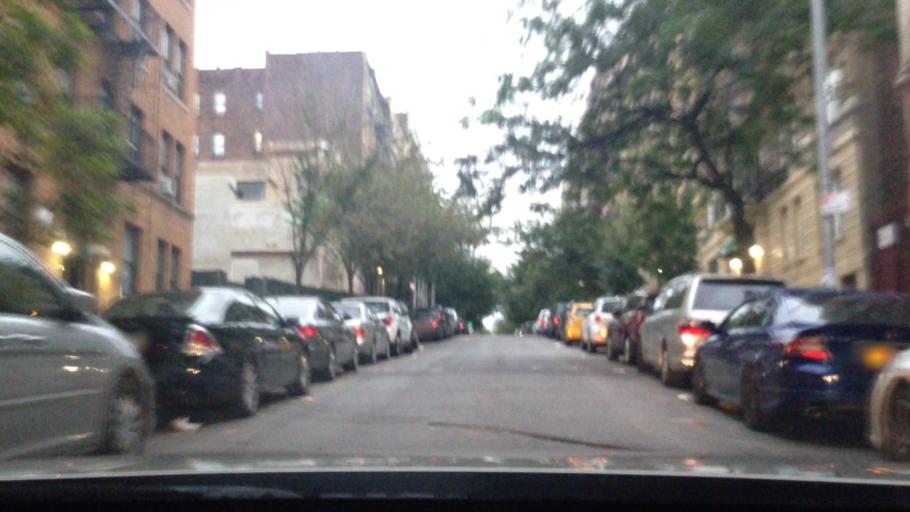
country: US
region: New Jersey
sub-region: Bergen County
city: Edgewater
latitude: 40.8315
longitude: -73.9490
